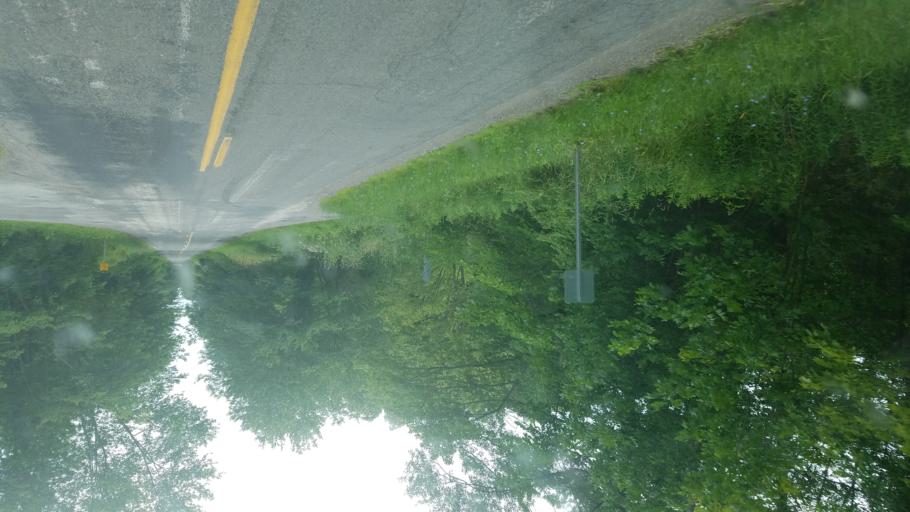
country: US
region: Ohio
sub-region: Trumbull County
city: Cortland
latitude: 41.4191
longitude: -80.7770
